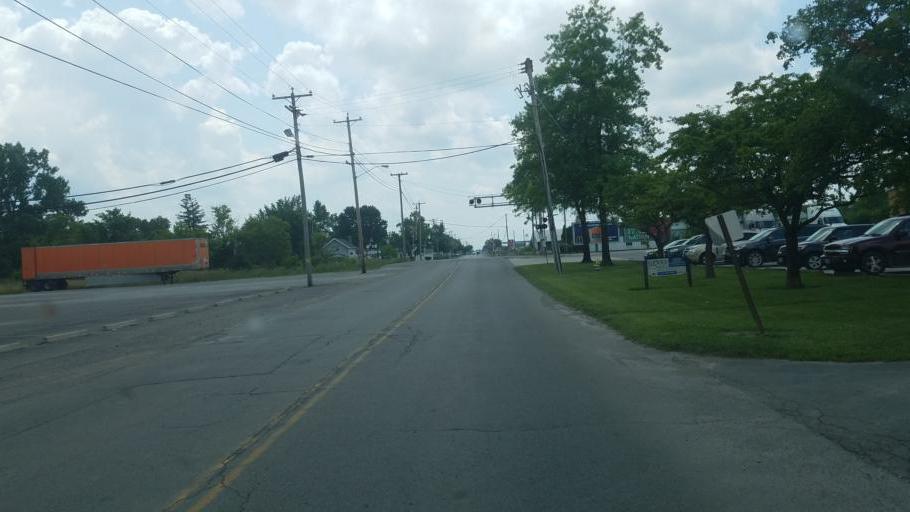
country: US
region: Ohio
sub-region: Hardin County
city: Kenton
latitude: 40.6385
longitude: -83.6113
